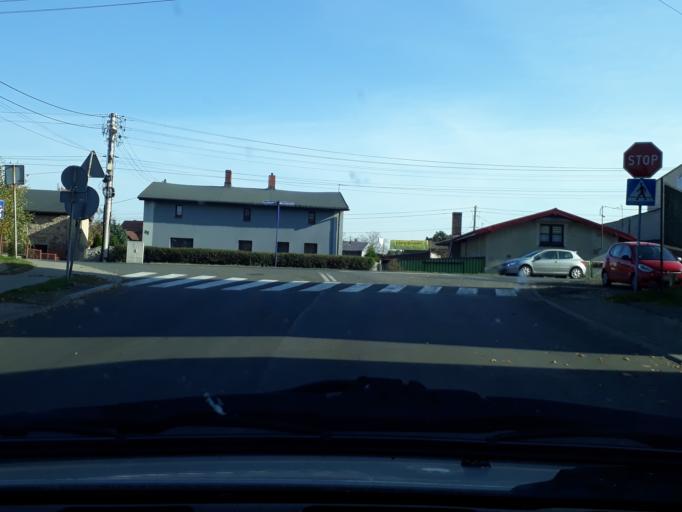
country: PL
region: Silesian Voivodeship
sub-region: Powiat tarnogorski
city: Tarnowskie Gory
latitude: 50.4234
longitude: 18.8672
